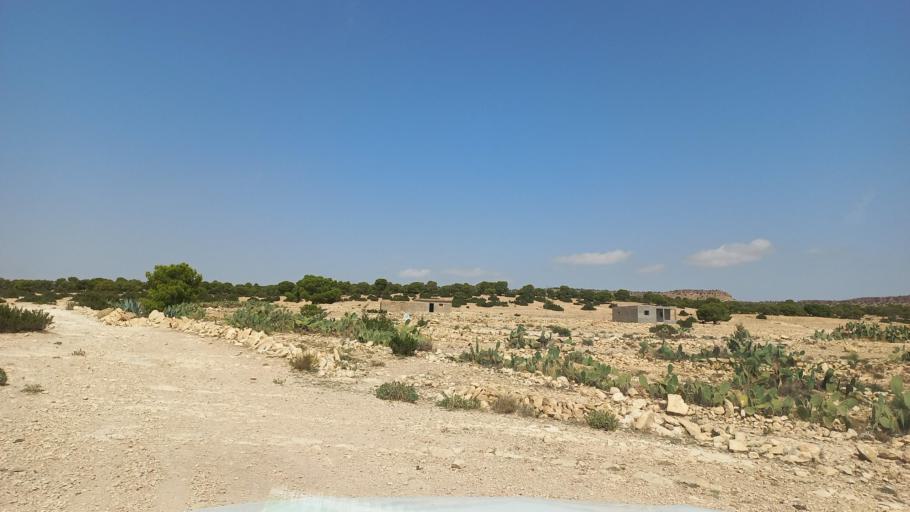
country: TN
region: Al Qasrayn
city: Sbiba
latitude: 35.4022
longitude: 8.9656
